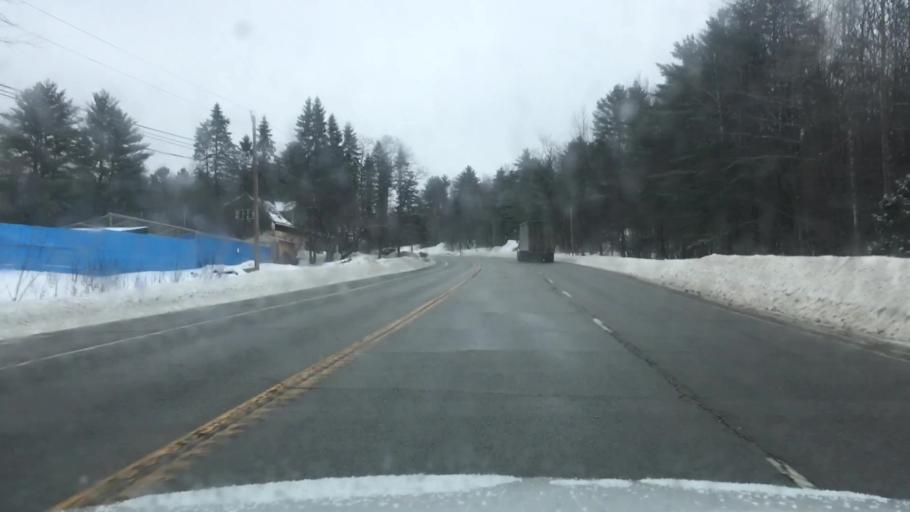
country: US
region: Maine
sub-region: Oxford County
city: Peru
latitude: 44.5737
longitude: -70.3711
